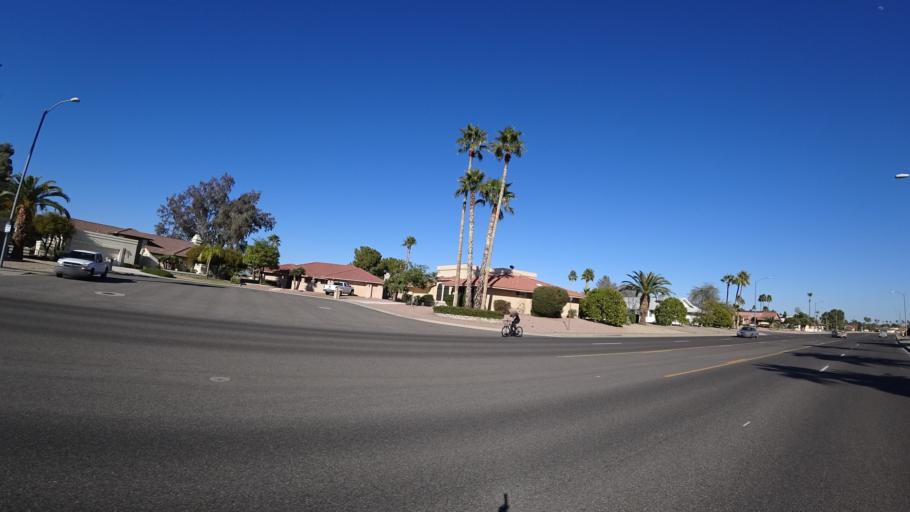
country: US
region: Arizona
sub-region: Maricopa County
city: Sun City West
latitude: 33.6788
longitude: -112.3523
